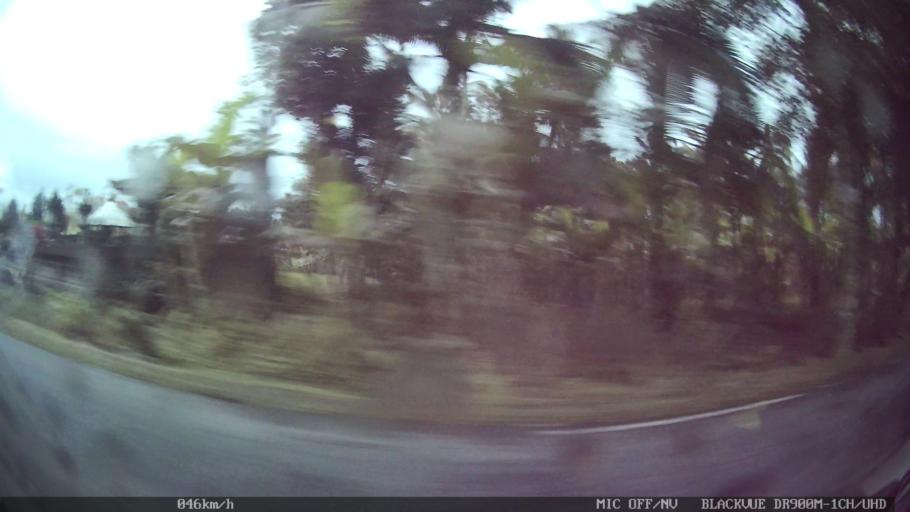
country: ID
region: Bali
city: Banjar Ponggang
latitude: -8.3923
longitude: 115.2565
